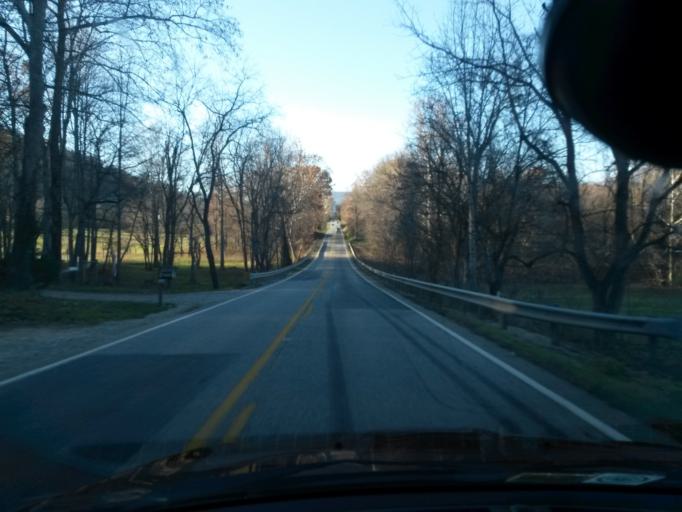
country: US
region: Virginia
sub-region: Amherst County
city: Amherst
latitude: 37.6456
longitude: -79.1264
